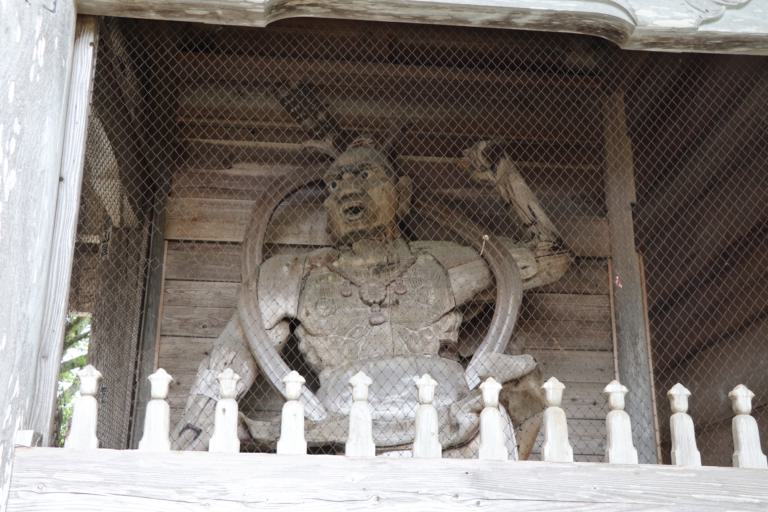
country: JP
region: Iwate
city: Tono
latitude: 39.3546
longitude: 141.5716
